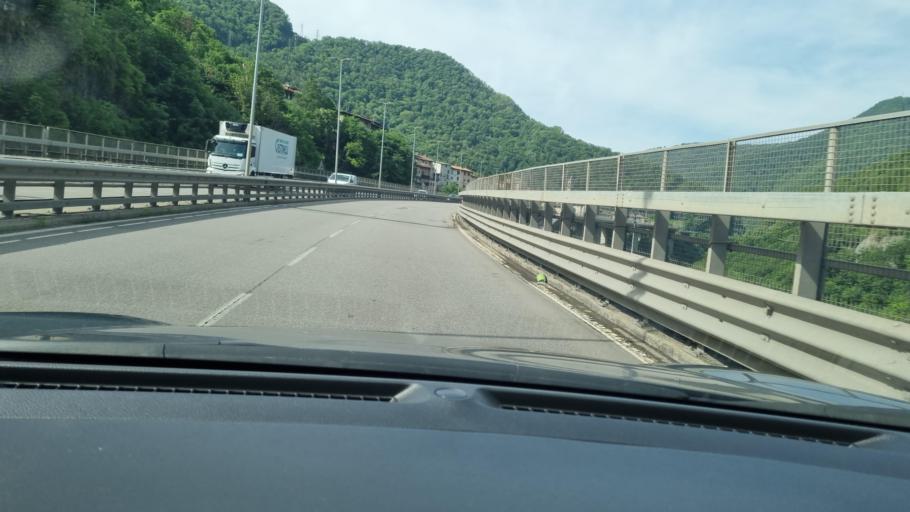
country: IT
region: Lombardy
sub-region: Provincia di Bergamo
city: Sedrina
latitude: 45.7857
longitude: 9.6292
